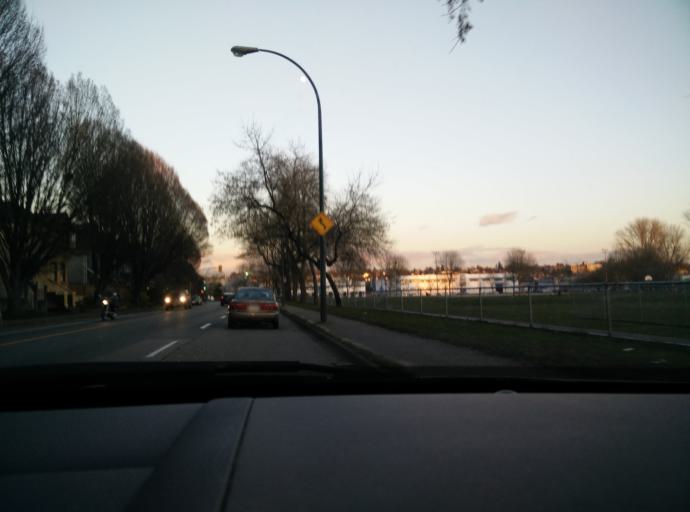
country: CA
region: British Columbia
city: Vancouver
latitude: 49.2765
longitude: -123.0866
